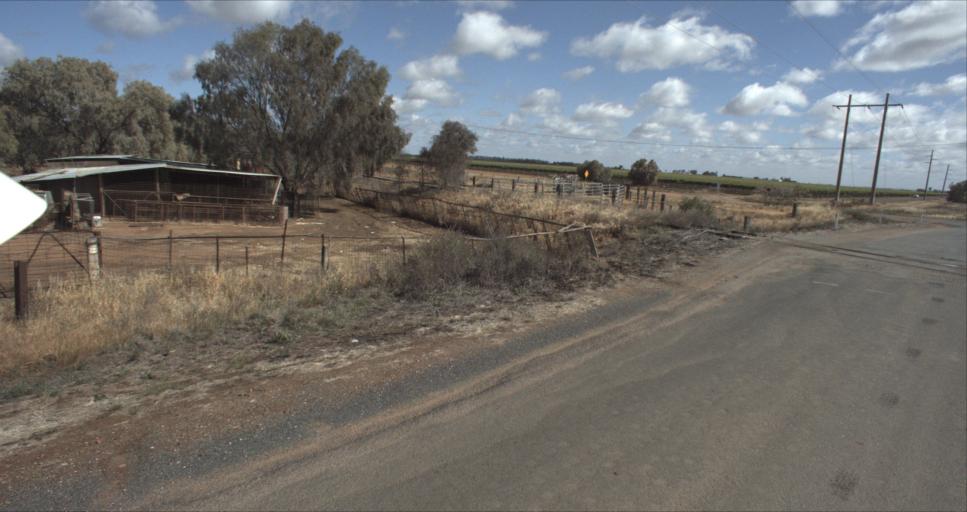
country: AU
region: New South Wales
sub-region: Murrumbidgee Shire
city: Darlington Point
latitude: -34.5142
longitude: 146.1769
